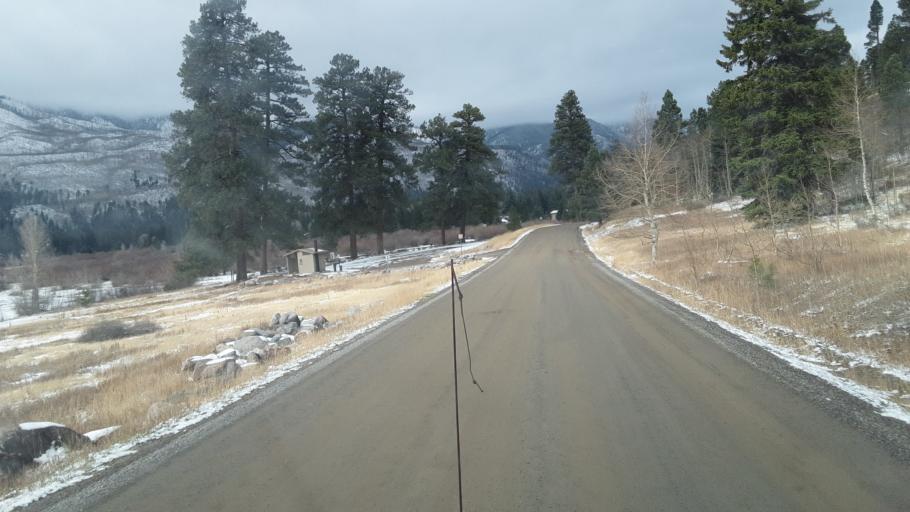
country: US
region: Colorado
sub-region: La Plata County
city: Bayfield
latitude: 37.4317
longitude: -107.5417
